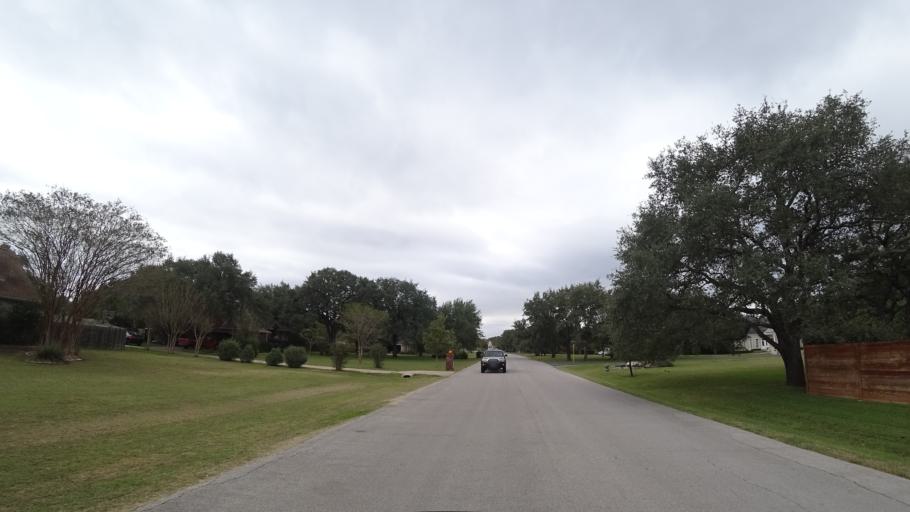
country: US
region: Texas
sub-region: Travis County
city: Shady Hollow
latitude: 30.1552
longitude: -97.8630
